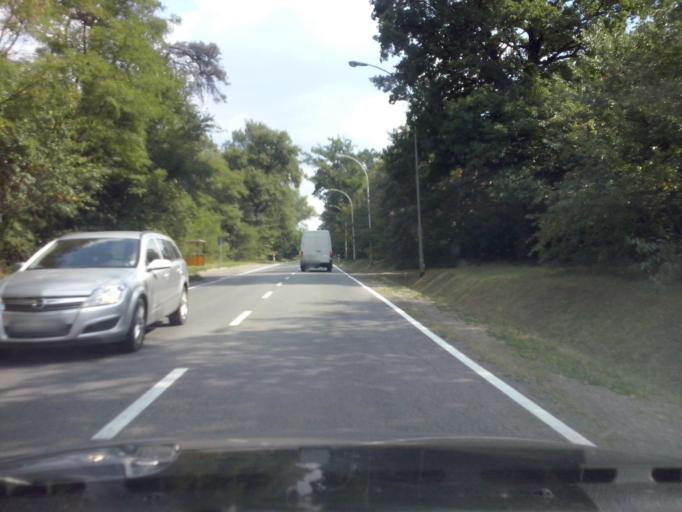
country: PL
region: Subcarpathian Voivodeship
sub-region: Powiat nizanski
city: Rudnik nad Sanem
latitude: 50.4333
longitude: 22.2663
